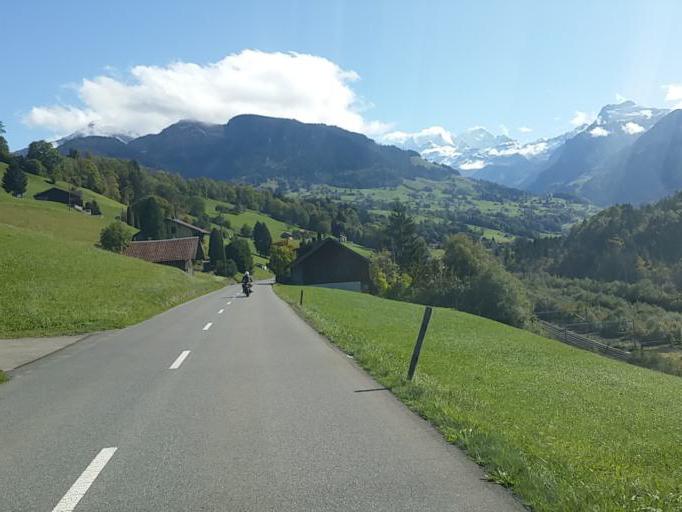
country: CH
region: Bern
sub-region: Frutigen-Niedersimmental District
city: Aeschi
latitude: 46.6529
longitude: 7.6855
